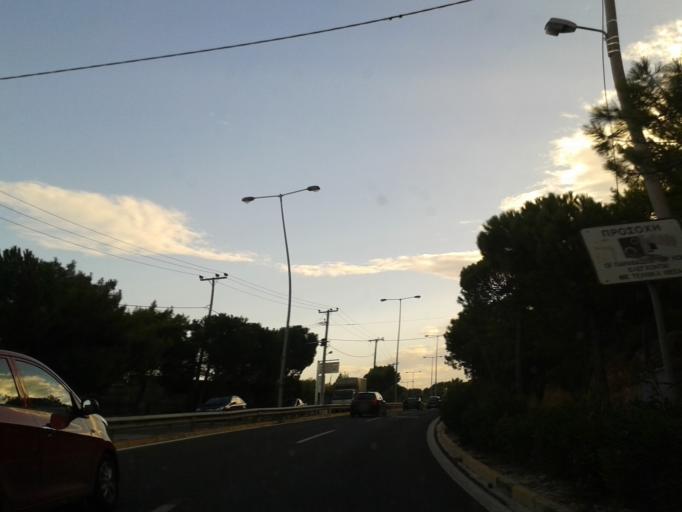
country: GR
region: Attica
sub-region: Nomarchia Anatolikis Attikis
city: Neos Voutzas
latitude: 38.0393
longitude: 23.9903
